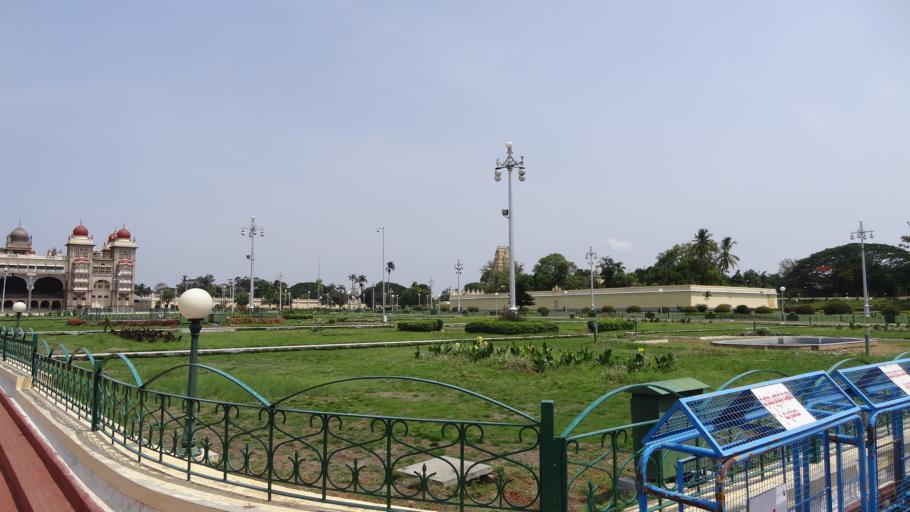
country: IN
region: Karnataka
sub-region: Mysore
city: Mysore
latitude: 12.3050
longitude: 76.6570
